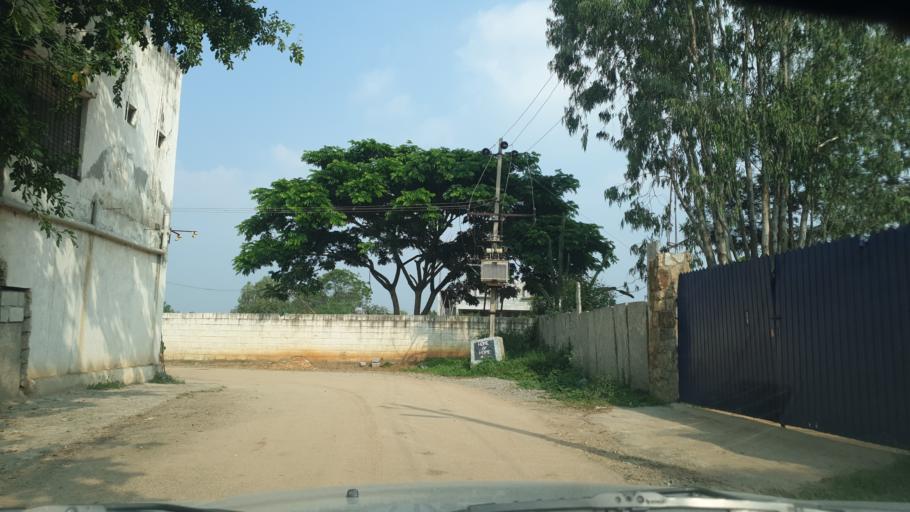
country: IN
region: Karnataka
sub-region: Bangalore Urban
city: Yelahanka
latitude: 13.0703
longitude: 77.6598
